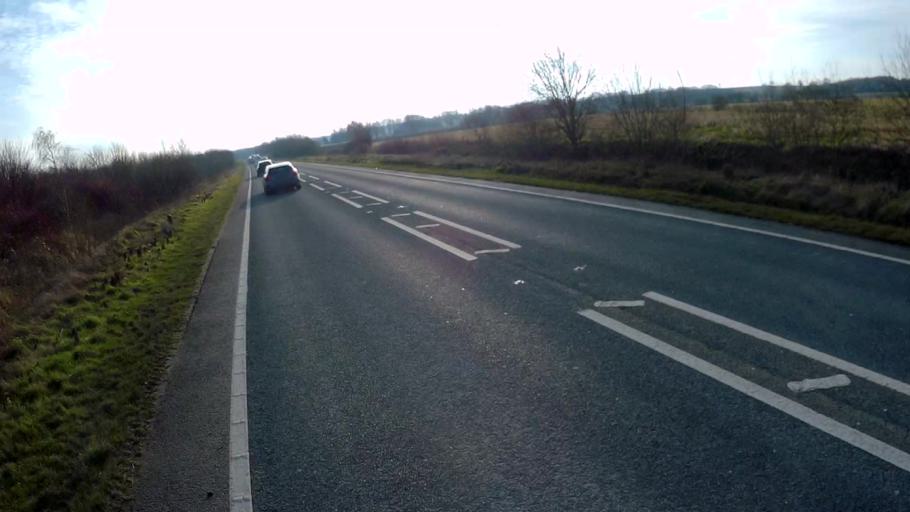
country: GB
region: England
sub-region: Lincolnshire
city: Bourne
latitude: 52.7627
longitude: -0.3952
